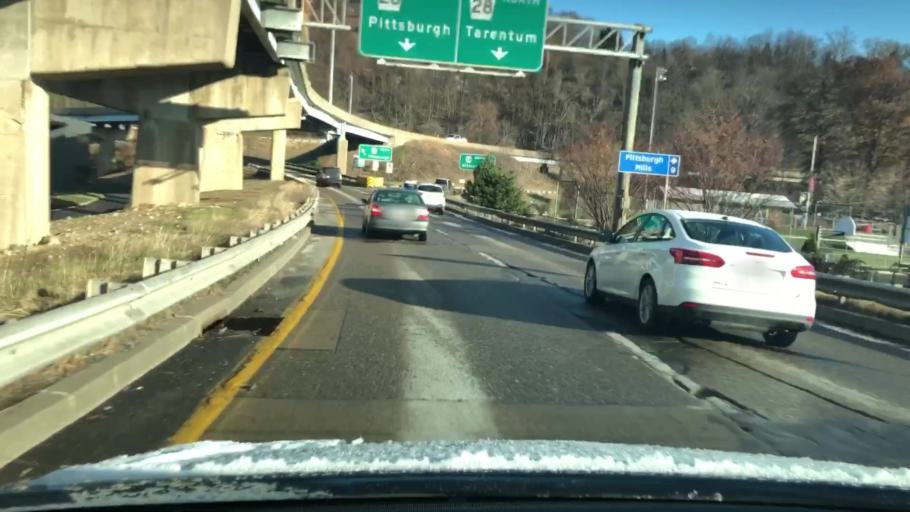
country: US
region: Pennsylvania
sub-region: Allegheny County
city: Aspinwall
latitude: 40.4938
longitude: -79.9092
